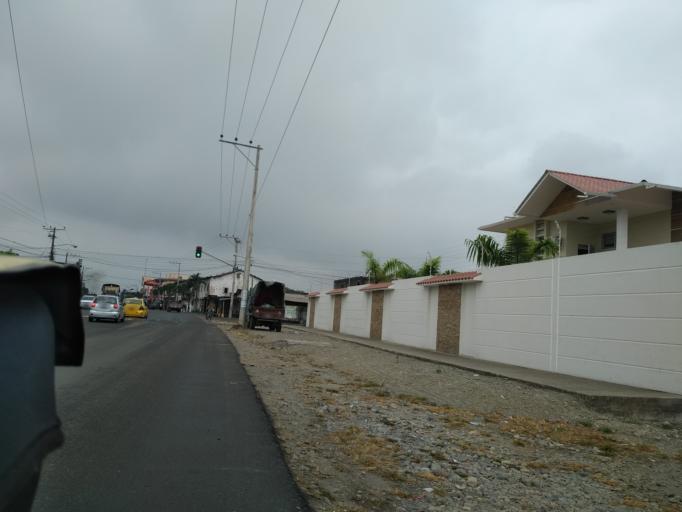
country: EC
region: Cotopaxi
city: La Mana
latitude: -0.9455
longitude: -79.3337
